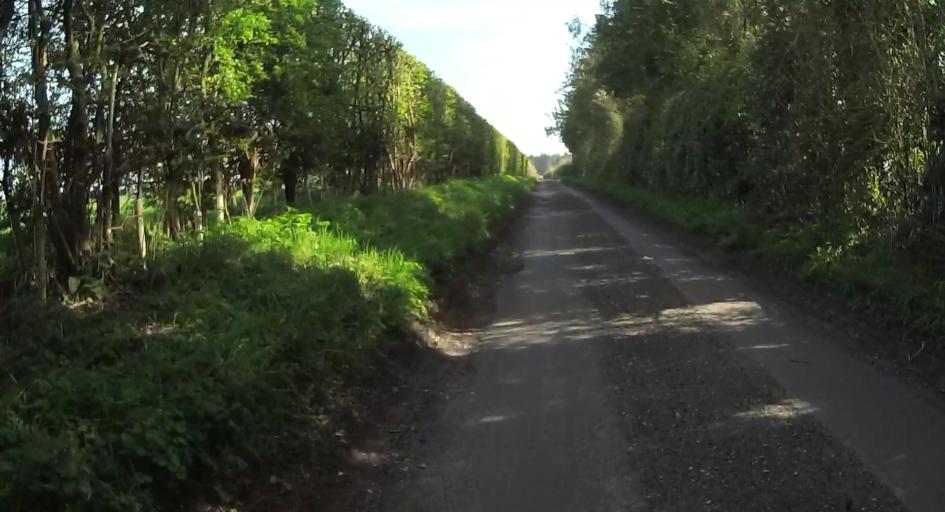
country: GB
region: England
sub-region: Hampshire
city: Highclere
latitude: 51.2612
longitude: -1.3690
